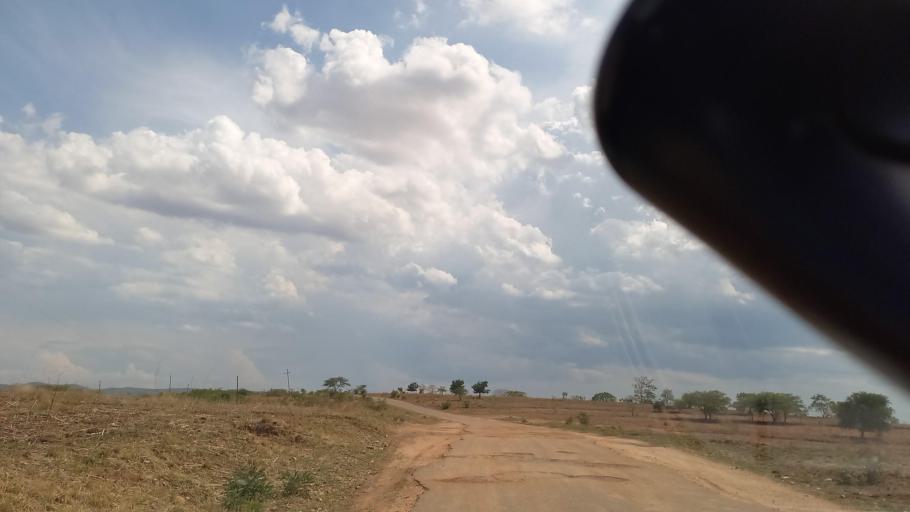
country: ZM
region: Lusaka
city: Kafue
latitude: -16.1836
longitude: 28.0873
